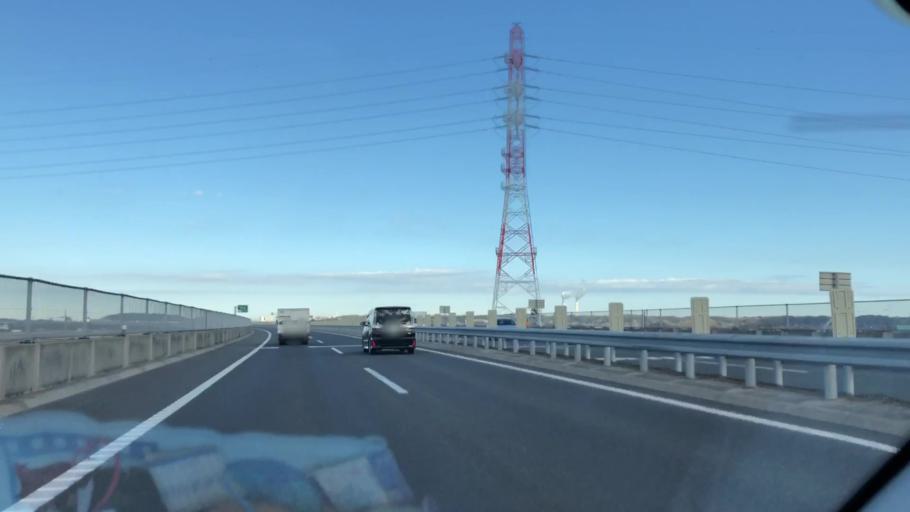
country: JP
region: Chiba
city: Kisarazu
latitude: 35.3989
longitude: 139.9673
